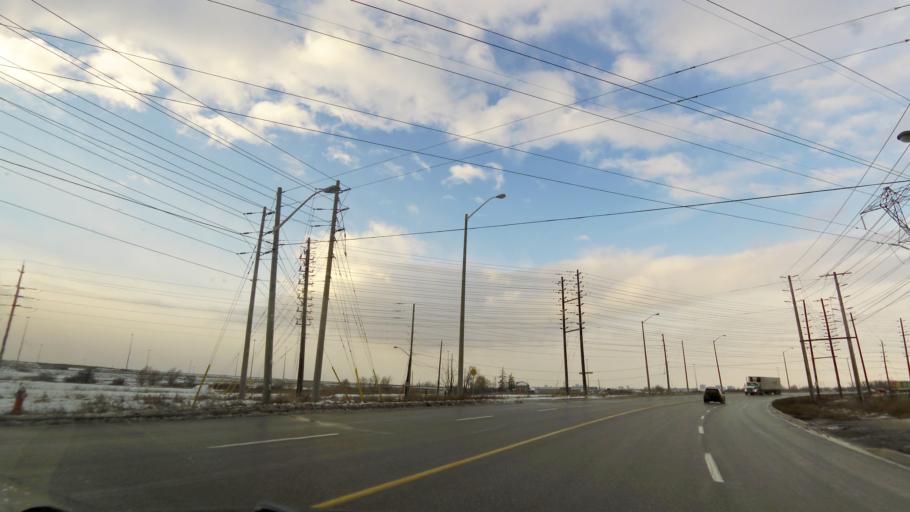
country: CA
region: Ontario
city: Brampton
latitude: 43.6712
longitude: -79.6920
